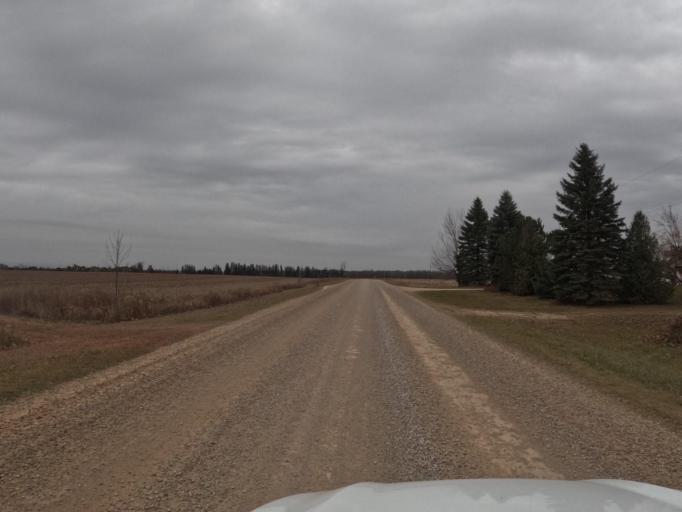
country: CA
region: Ontario
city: Shelburne
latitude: 43.8716
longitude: -80.3559
